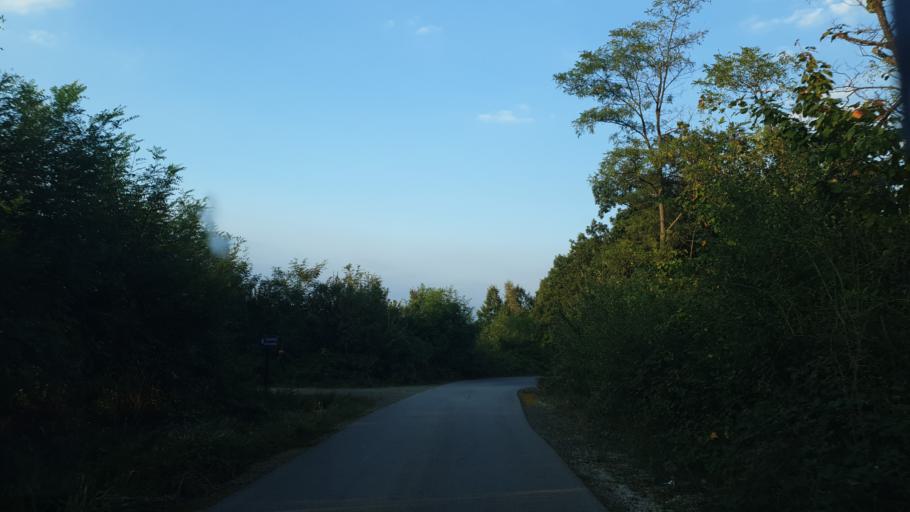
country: RS
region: Central Serbia
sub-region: Zlatiborski Okrug
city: Kosjeric
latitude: 44.0260
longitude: 20.0074
